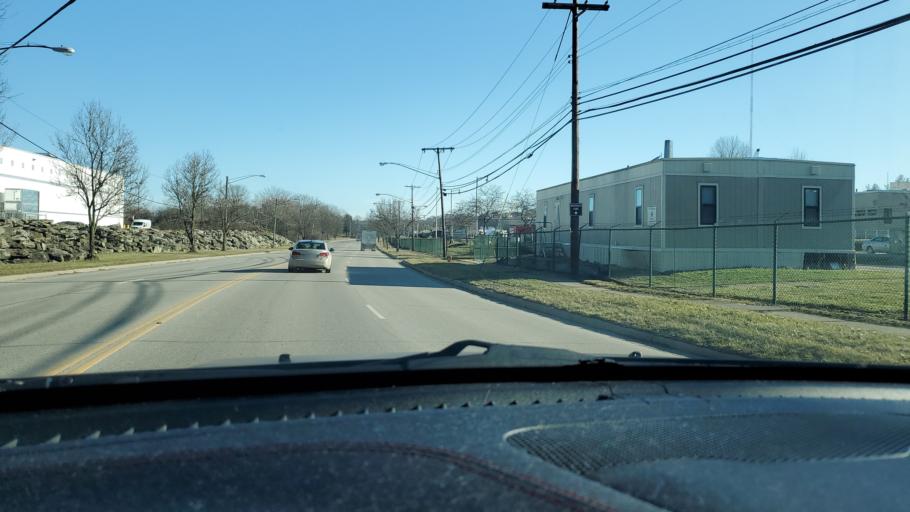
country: US
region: Ohio
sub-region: Mahoning County
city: Youngstown
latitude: 41.0920
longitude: -80.6423
